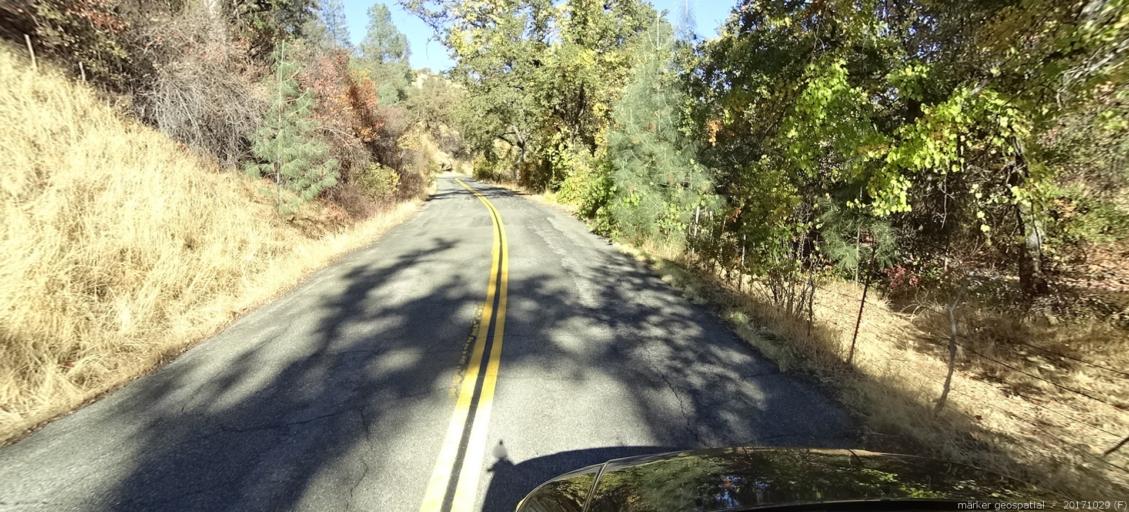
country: US
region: California
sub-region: Trinity County
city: Lewiston
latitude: 40.4077
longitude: -122.7702
